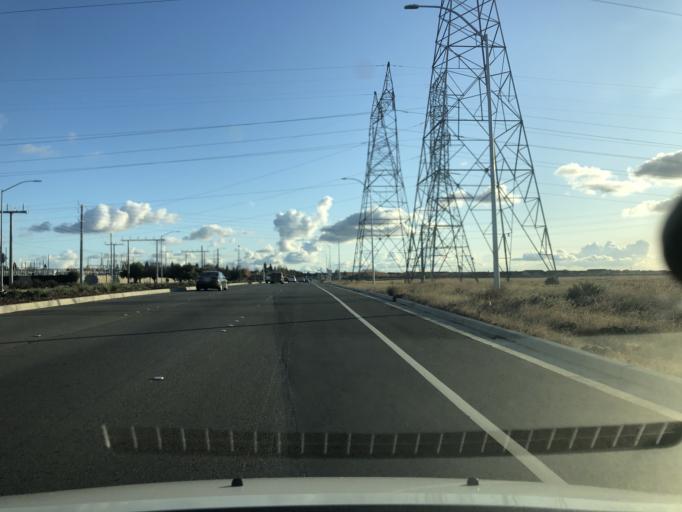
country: US
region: California
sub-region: Sacramento County
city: Antelope
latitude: 38.7653
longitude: -121.3587
